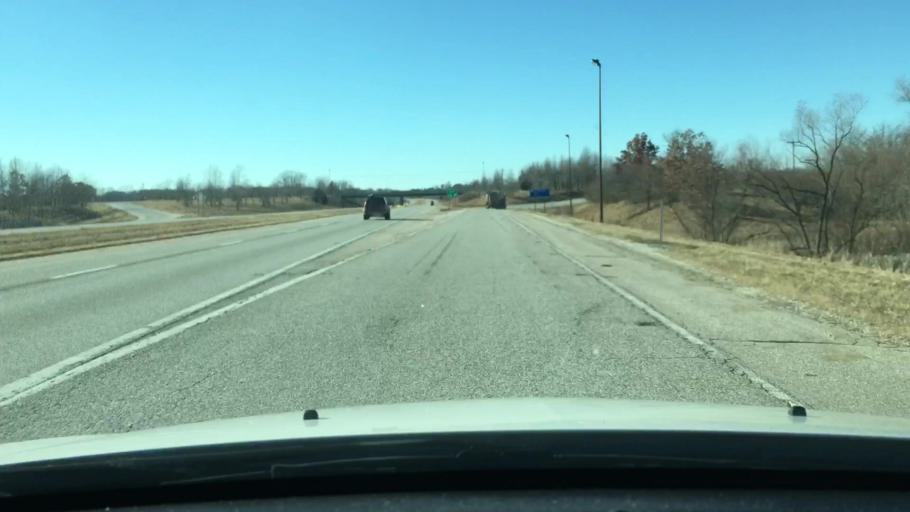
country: US
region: Illinois
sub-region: Pike County
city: Griggsville
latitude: 39.6743
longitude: -90.7632
